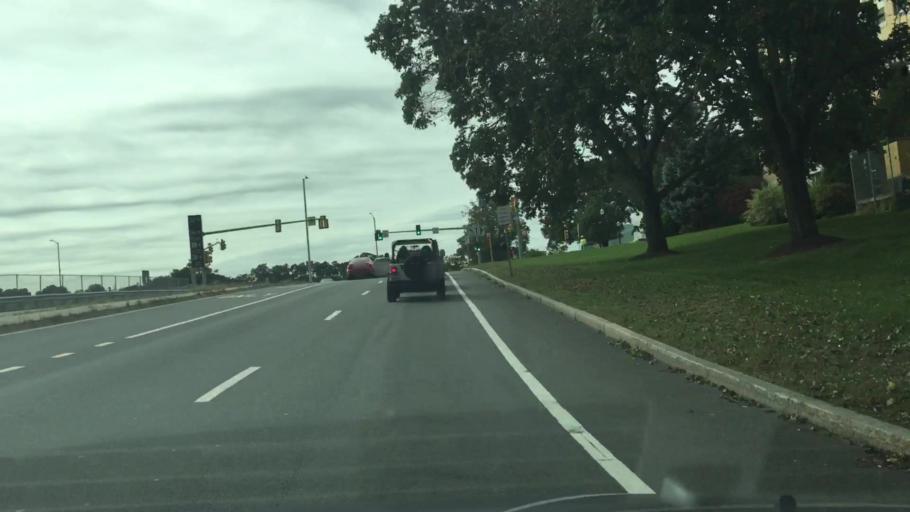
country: US
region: Massachusetts
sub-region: Middlesex County
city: Dracut
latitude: 42.6572
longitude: -71.3219
